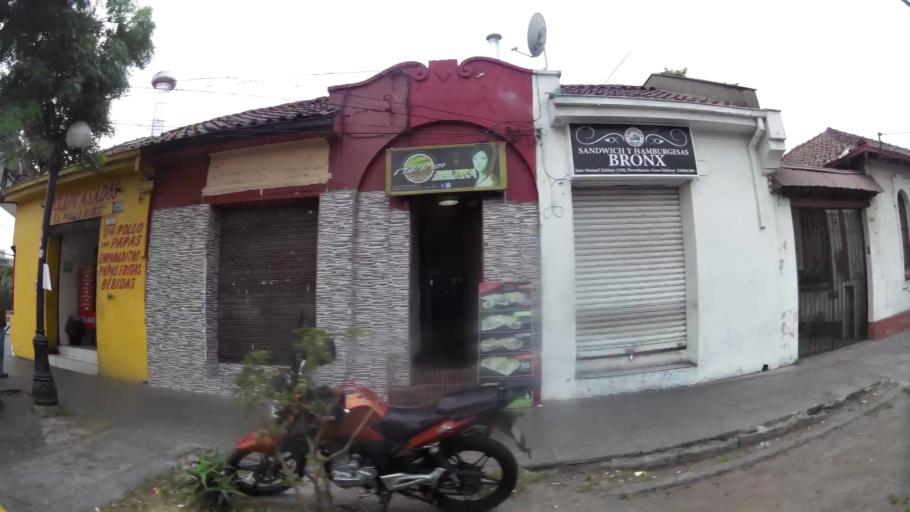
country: CL
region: Santiago Metropolitan
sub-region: Provincia de Santiago
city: Santiago
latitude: -33.4452
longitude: -70.6193
